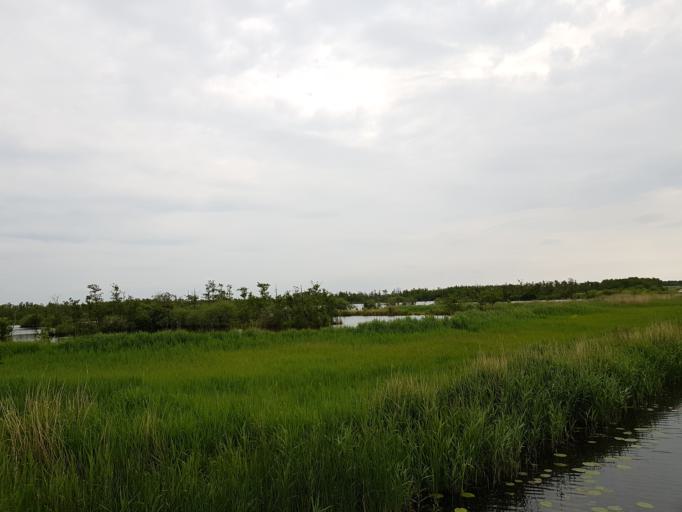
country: NL
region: Friesland
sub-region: Gemeente Boarnsterhim
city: Warten
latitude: 53.1419
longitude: 5.9295
